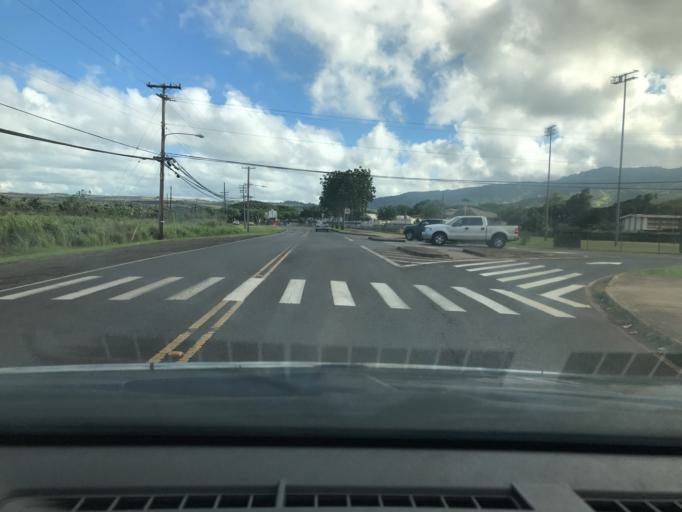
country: US
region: Hawaii
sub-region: Honolulu County
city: Waialua
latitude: 21.5778
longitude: -158.1228
